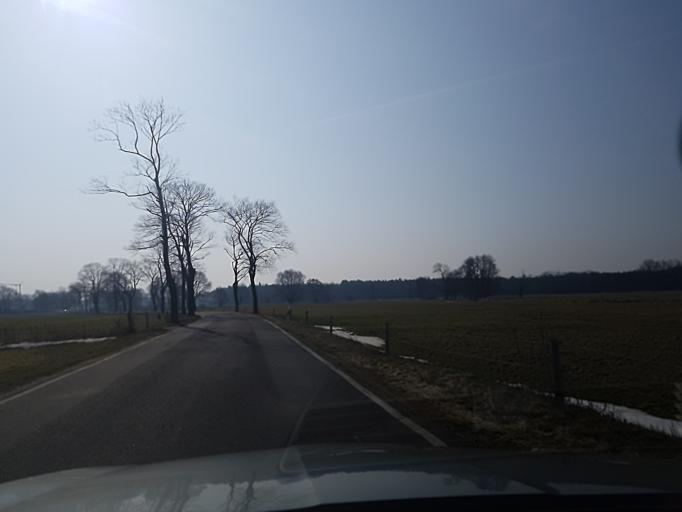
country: DE
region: Brandenburg
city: Falkenberg
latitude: 51.6390
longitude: 13.2706
